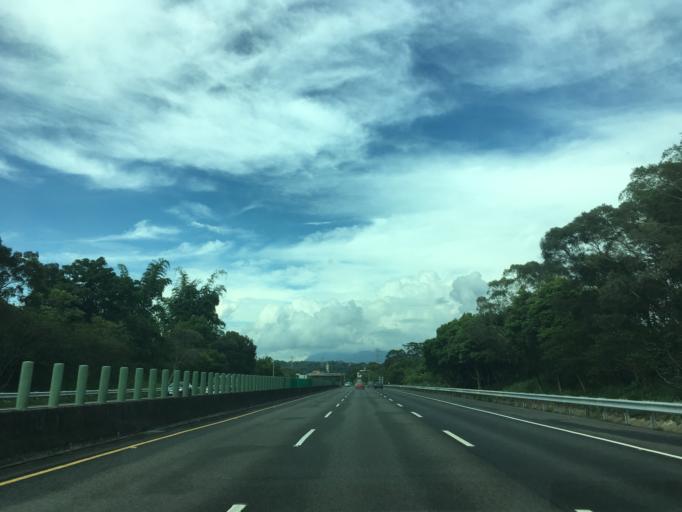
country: TW
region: Taiwan
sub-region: Chiayi
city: Jiayi Shi
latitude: 23.4585
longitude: 120.4915
